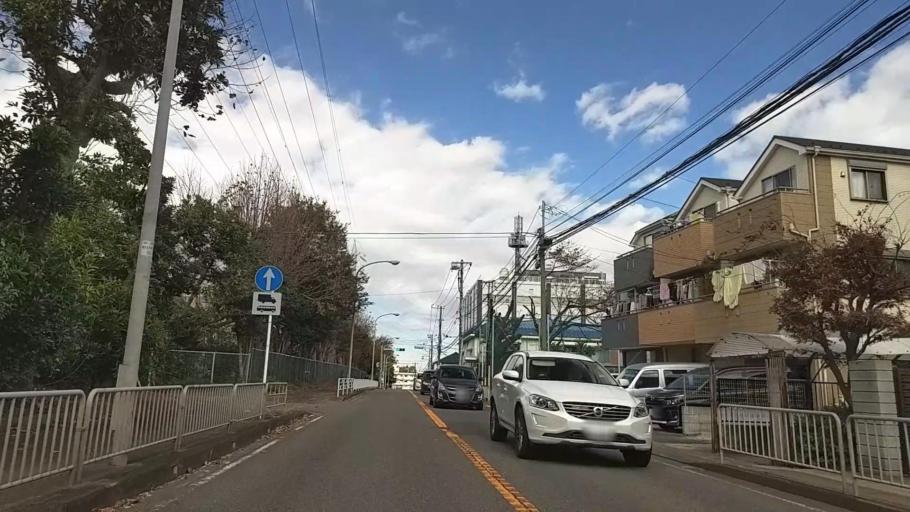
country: JP
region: Kanagawa
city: Yokohama
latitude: 35.4977
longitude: 139.6367
